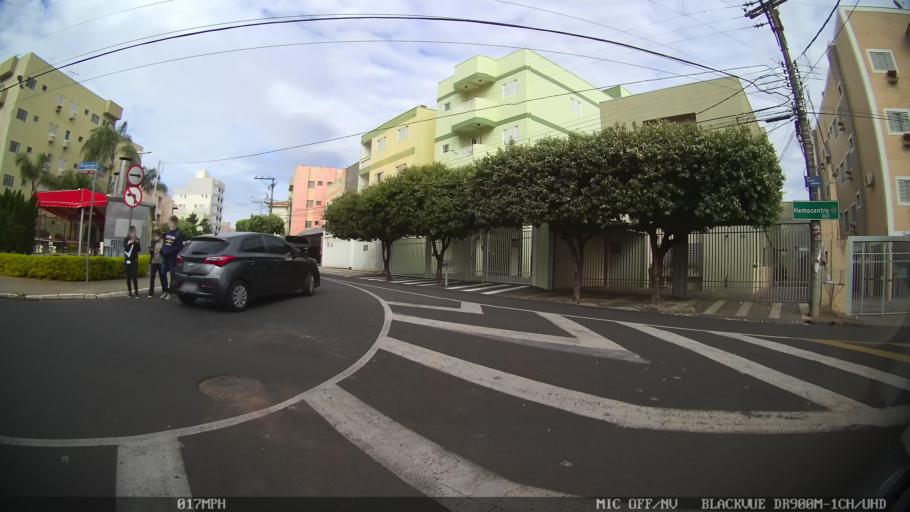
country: BR
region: Sao Paulo
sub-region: Sao Jose Do Rio Preto
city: Sao Jose do Rio Preto
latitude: -20.8281
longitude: -49.3996
